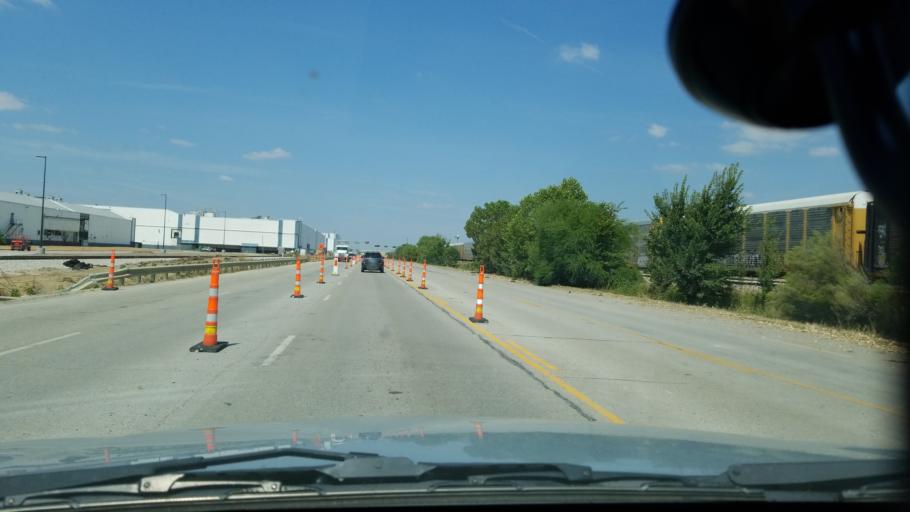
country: US
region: Texas
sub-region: Dallas County
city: Grand Prairie
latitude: 32.7456
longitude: -96.9774
